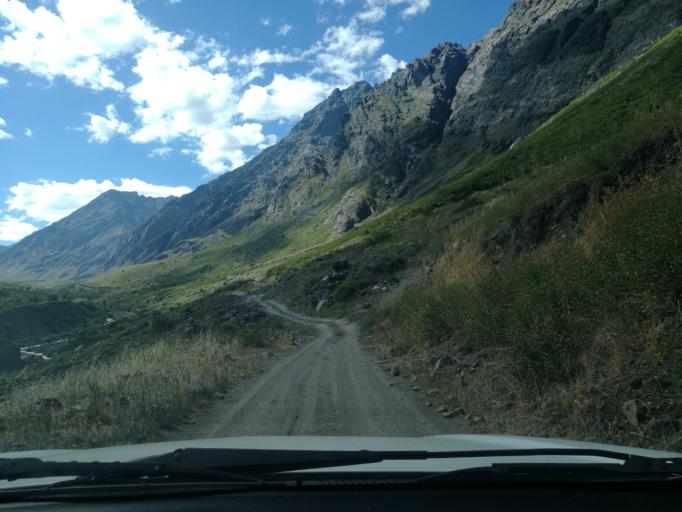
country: CL
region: O'Higgins
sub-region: Provincia de Cachapoal
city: Machali
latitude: -34.3914
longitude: -70.2766
